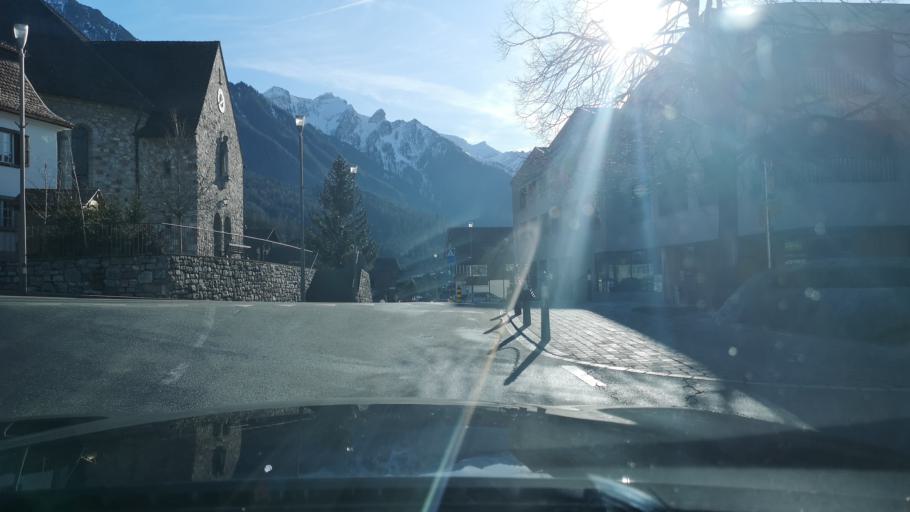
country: LI
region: Triesenberg
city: Triesenberg
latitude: 47.1188
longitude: 9.5431
